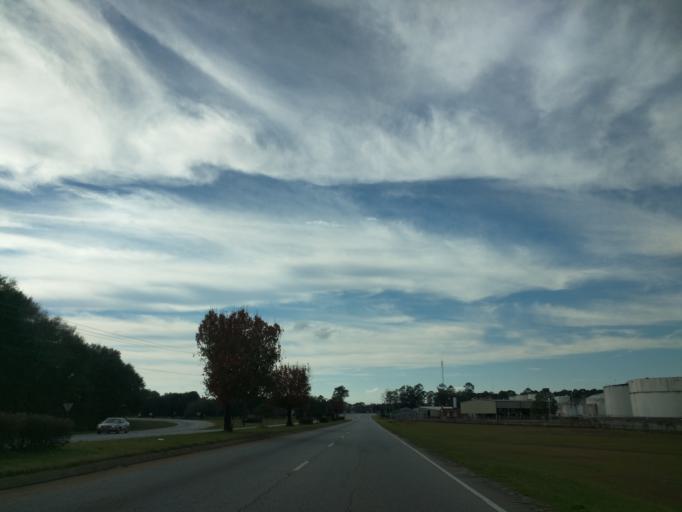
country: US
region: Georgia
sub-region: Decatur County
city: Bainbridge
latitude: 30.9032
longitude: -84.5393
